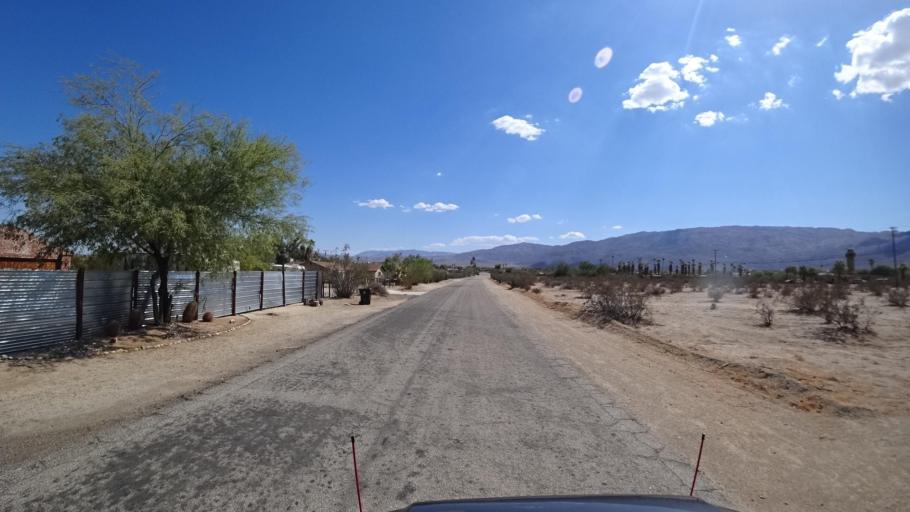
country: US
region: California
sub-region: San Diego County
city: Borrego Springs
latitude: 33.2479
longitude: -116.3727
